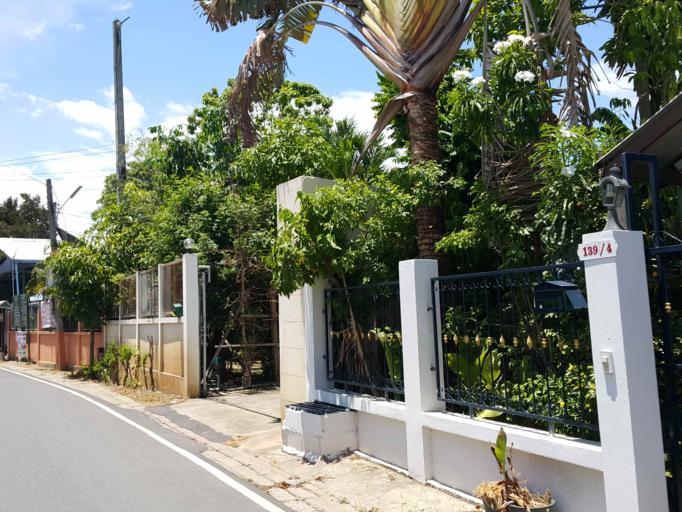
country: TH
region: Chiang Mai
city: Saraphi
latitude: 18.7470
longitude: 99.0149
